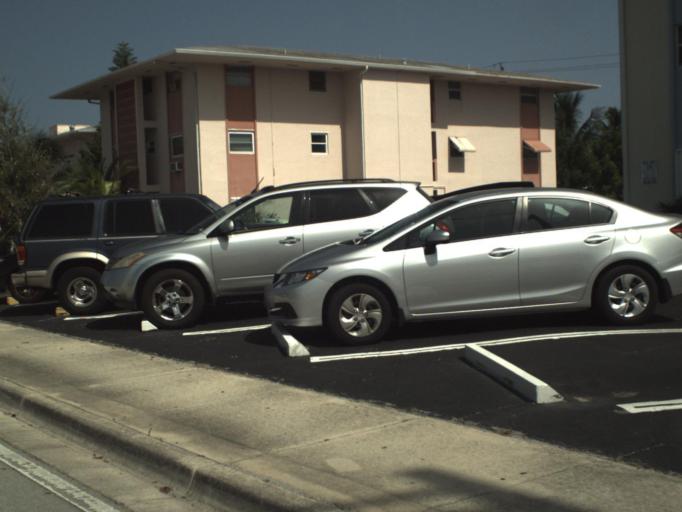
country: US
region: Florida
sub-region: Broward County
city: Pompano Beach Highlands
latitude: 26.2753
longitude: -80.1044
